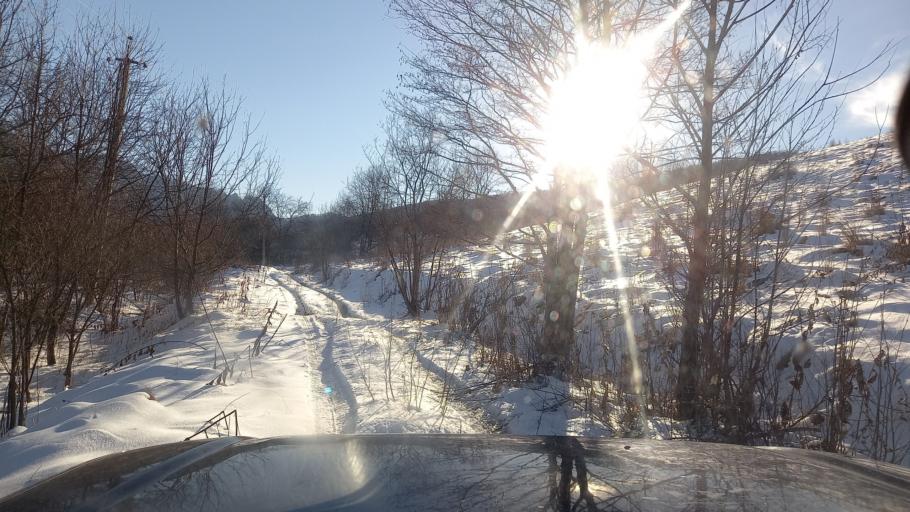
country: RU
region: Adygeya
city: Kamennomostskiy
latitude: 44.2010
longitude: 40.1502
